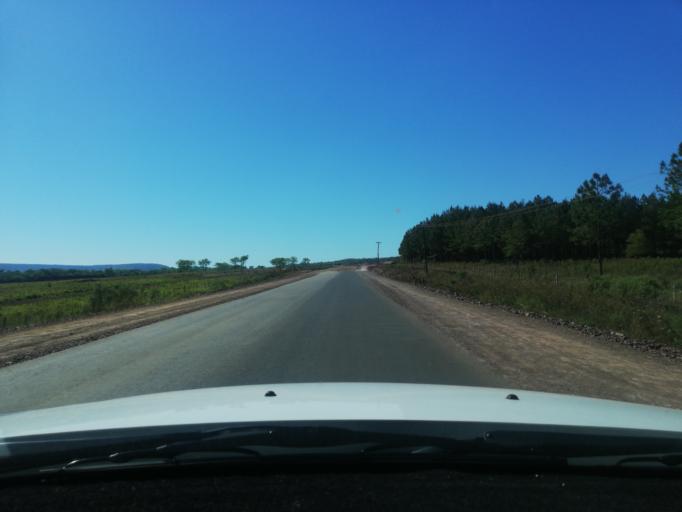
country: AR
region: Misiones
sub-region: Departamento de Candelaria
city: Candelaria
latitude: -27.5280
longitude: -55.7213
